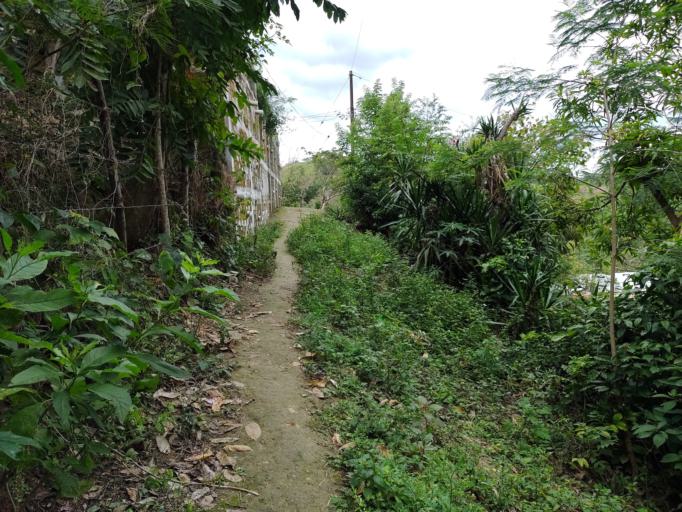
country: MX
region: Veracruz
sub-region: Papantla
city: Polutla
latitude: 20.4656
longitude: -97.2575
